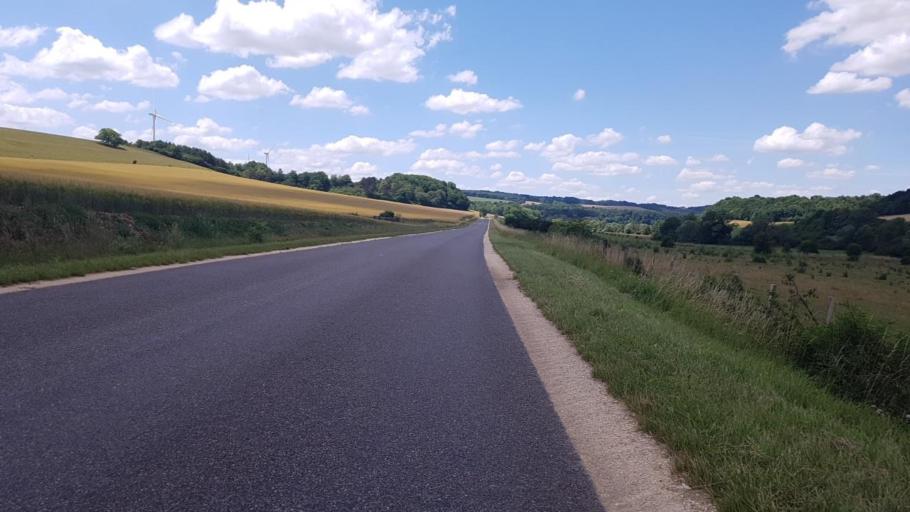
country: FR
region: Lorraine
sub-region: Departement de la Meuse
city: Vacon
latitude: 48.6343
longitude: 5.4930
